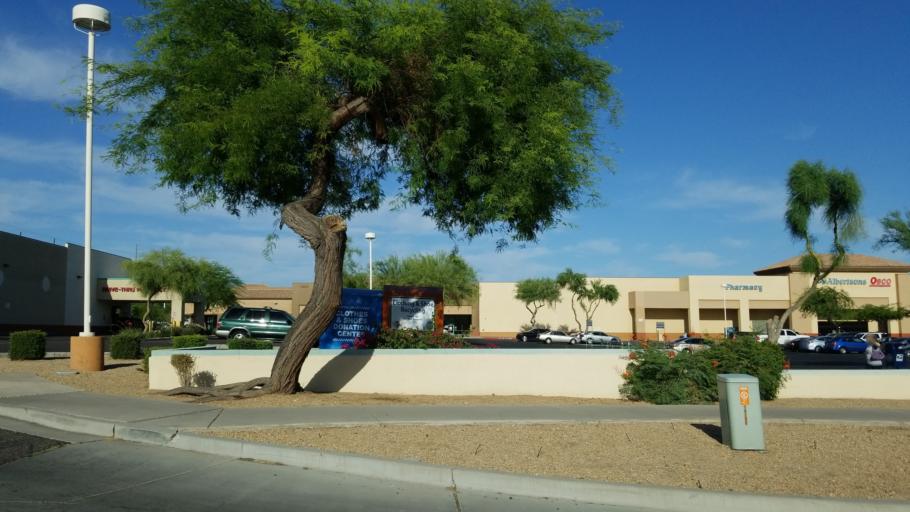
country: US
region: Arizona
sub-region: Maricopa County
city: Paradise Valley
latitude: 33.6538
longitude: -112.0308
